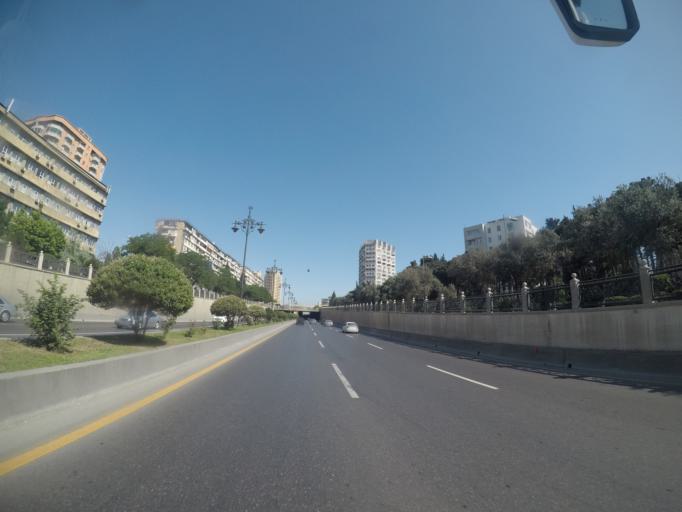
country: AZ
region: Baki
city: Bilajari
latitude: 40.4082
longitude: 49.8053
